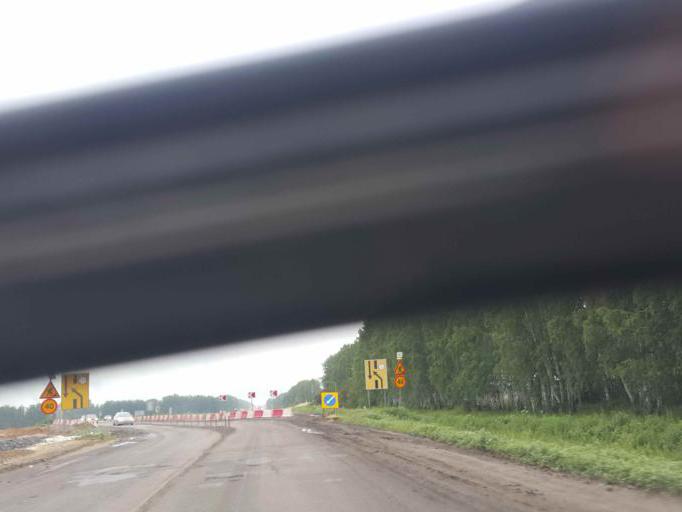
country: RU
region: Tambov
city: Selezni
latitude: 52.7889
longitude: 41.0187
